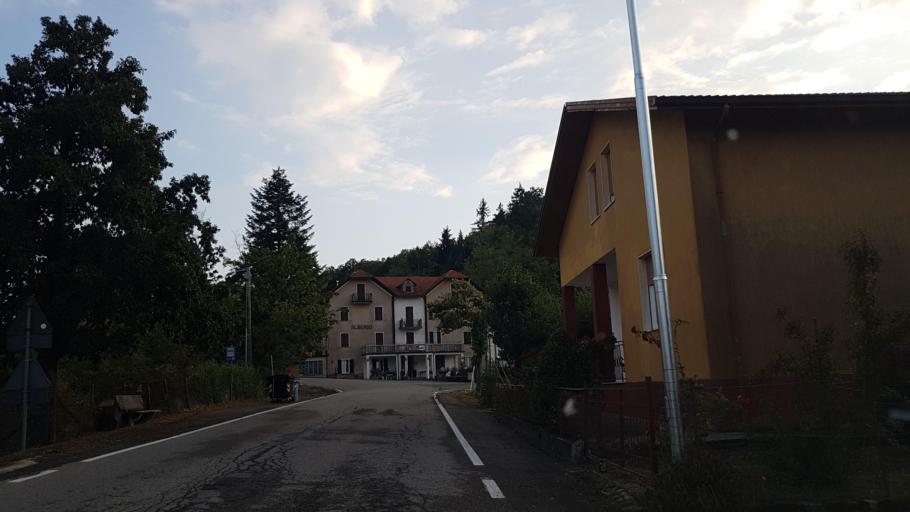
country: IT
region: Emilia-Romagna
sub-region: Provincia di Parma
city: Tornolo
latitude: 44.4389
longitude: 9.6352
